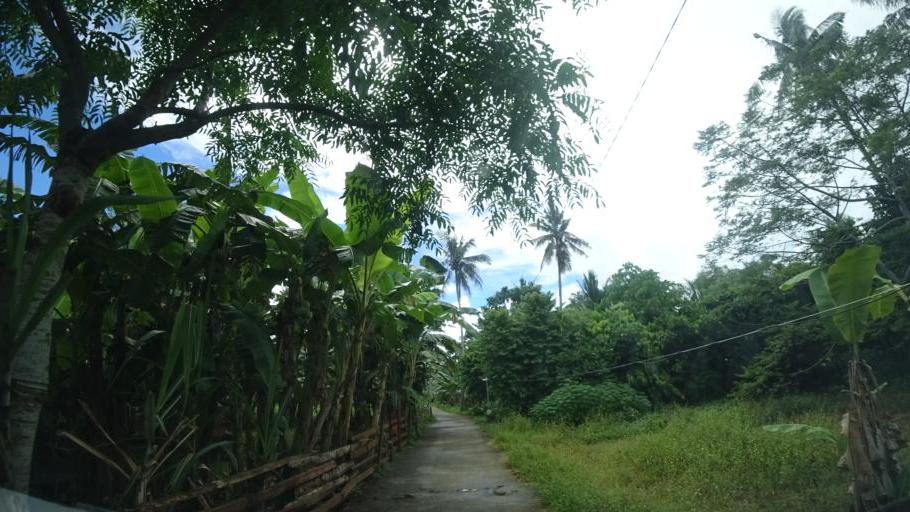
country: PH
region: Eastern Visayas
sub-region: Province of Leyte
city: Liberty
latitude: 10.8587
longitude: 124.9945
